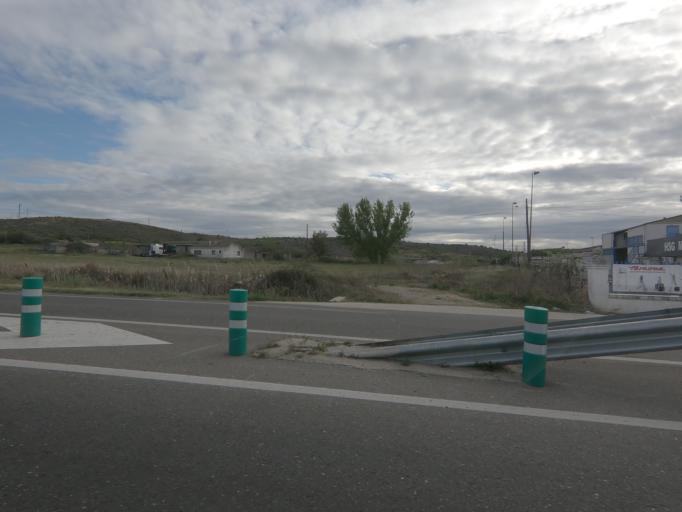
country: ES
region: Extremadura
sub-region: Provincia de Caceres
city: Coria
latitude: 39.9618
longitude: -6.5154
